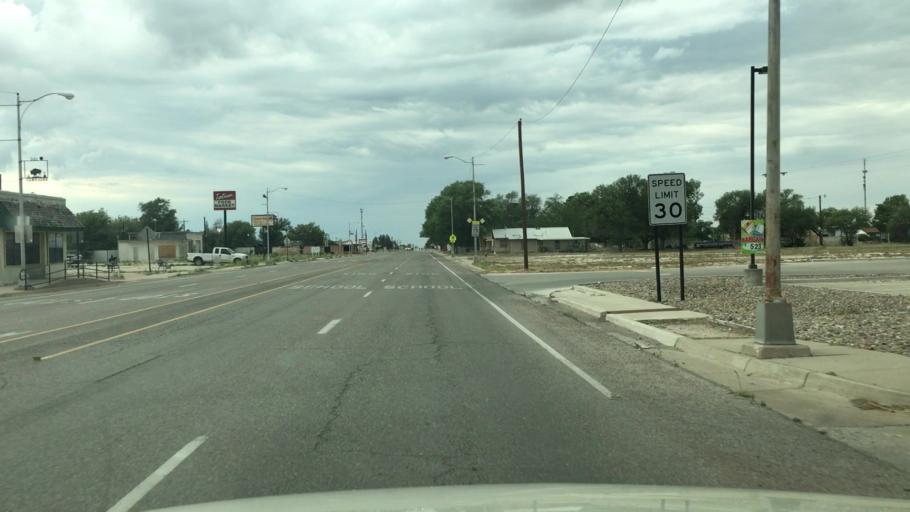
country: US
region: New Mexico
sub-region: Lea County
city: Lovington
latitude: 33.2570
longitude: -103.3190
